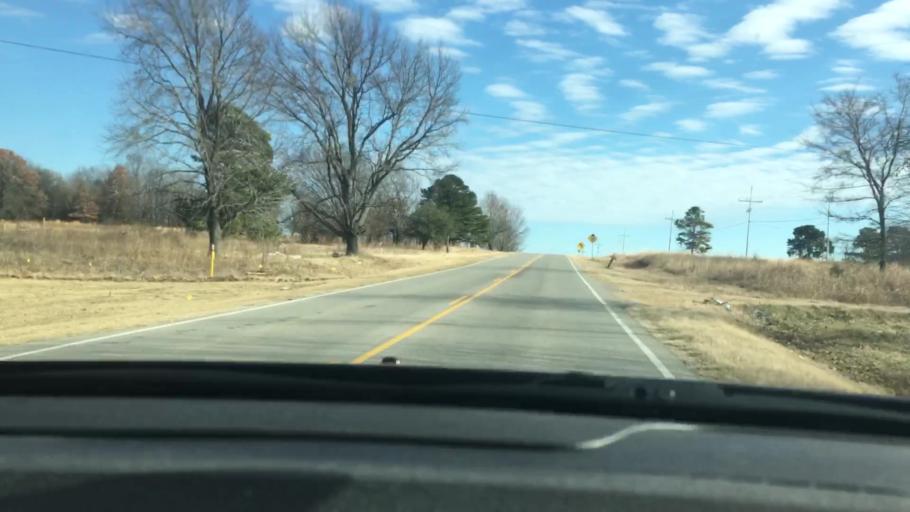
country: US
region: Oklahoma
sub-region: Pontotoc County
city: Ada
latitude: 34.7841
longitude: -96.7884
